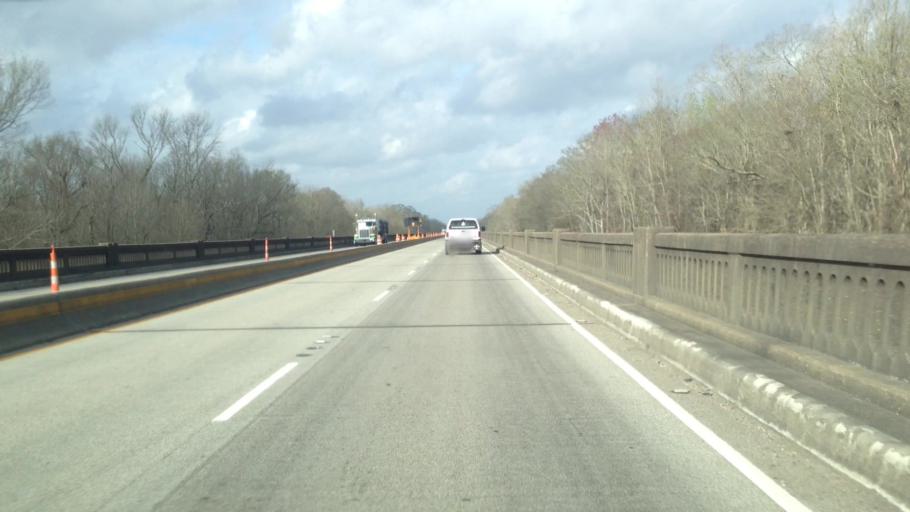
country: US
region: Louisiana
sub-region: Saint Landry Parish
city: Krotz Springs
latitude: 30.5560
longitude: -91.6703
